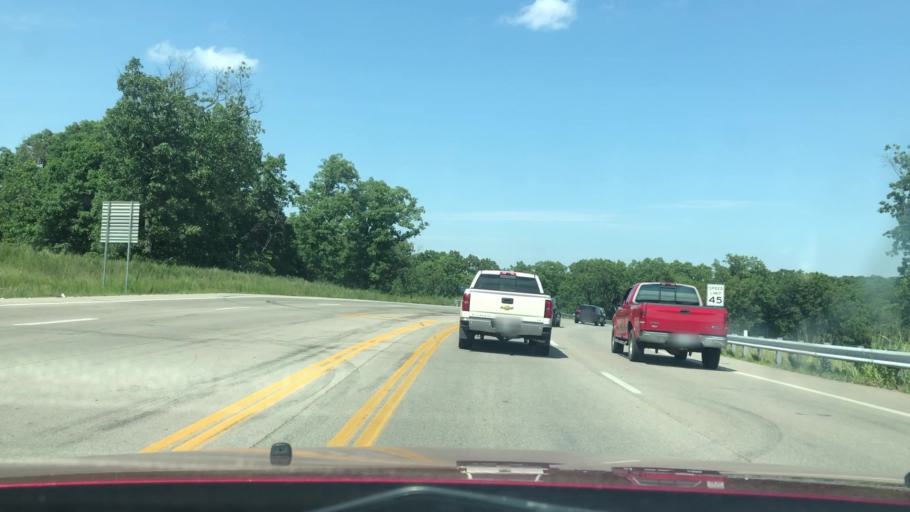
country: US
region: Missouri
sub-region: Stone County
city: Kimberling City
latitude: 36.6759
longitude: -93.3257
